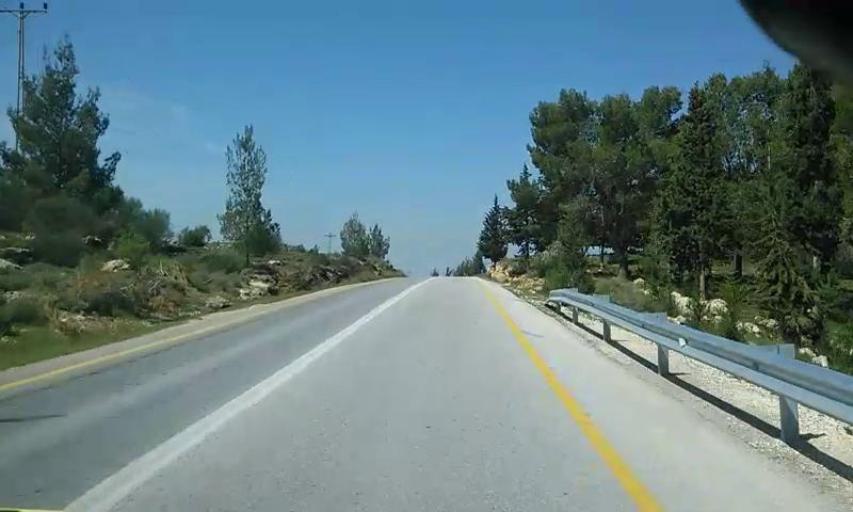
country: PS
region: West Bank
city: Nahhalin
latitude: 31.6739
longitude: 35.0925
